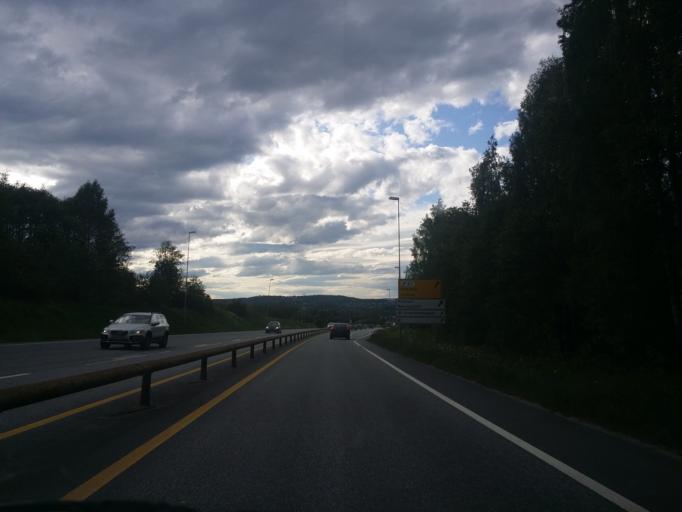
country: NO
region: Hedmark
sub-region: Hamar
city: Hamar
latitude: 60.7832
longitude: 11.1339
